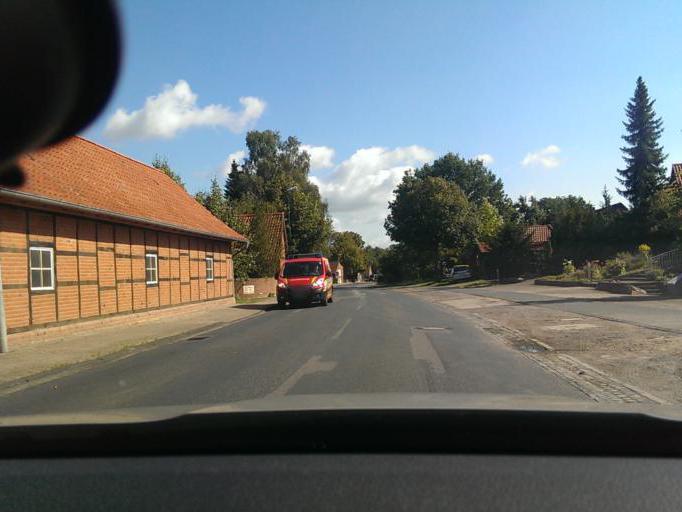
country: DE
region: Lower Saxony
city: Isernhagen Farster Bauerschaft
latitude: 52.4698
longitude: 9.8392
